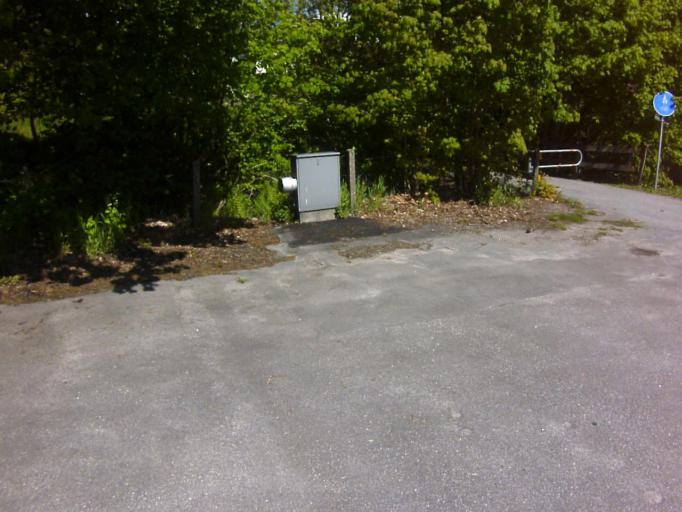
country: SE
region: Blekinge
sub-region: Solvesborgs Kommun
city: Soelvesborg
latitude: 56.0580
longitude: 14.6219
